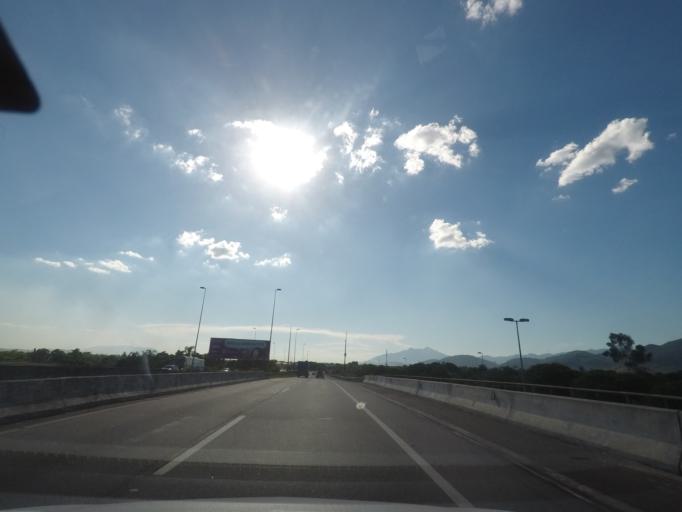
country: BR
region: Rio de Janeiro
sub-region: Petropolis
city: Petropolis
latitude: -22.6472
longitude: -43.2235
